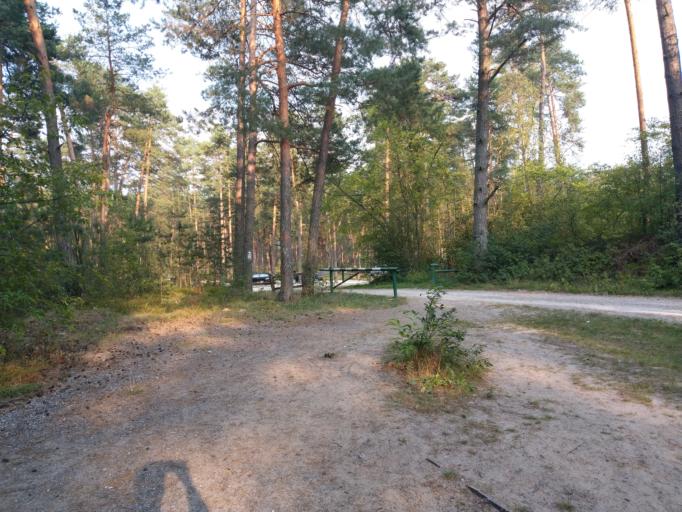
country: PL
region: Lublin Voivodeship
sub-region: Powiat bilgorajski
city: Jozefow
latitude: 50.4400
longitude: 23.1120
